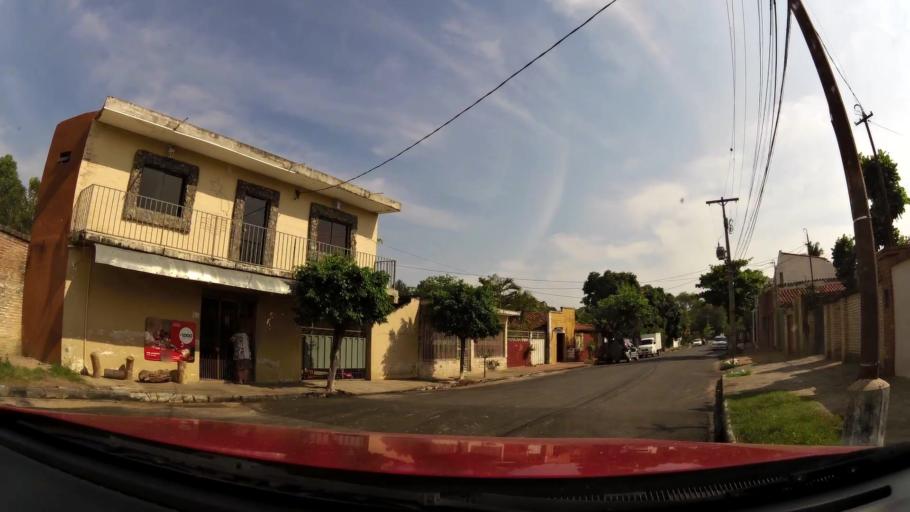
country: PY
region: Central
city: Fernando de la Mora
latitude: -25.2603
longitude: -57.5560
